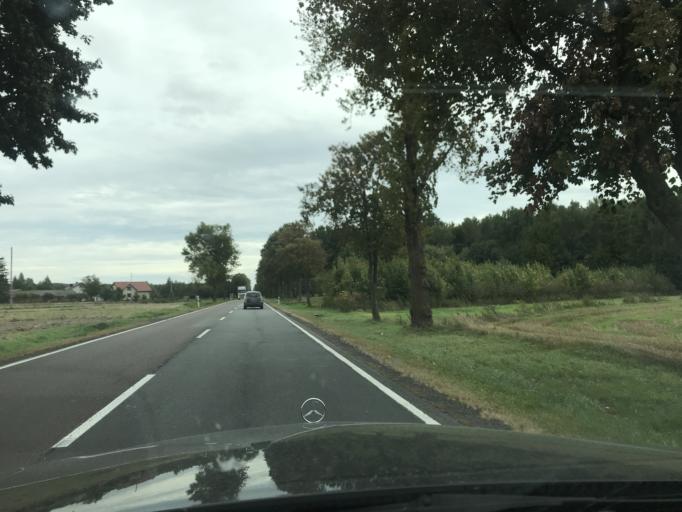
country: PL
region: Lublin Voivodeship
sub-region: Powiat krasnicki
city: Krasnik
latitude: 50.8743
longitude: 22.2679
